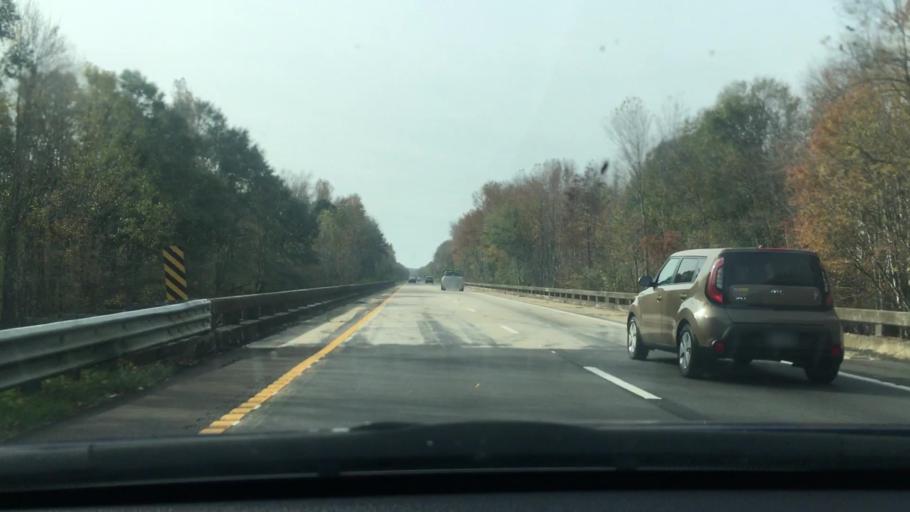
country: US
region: South Carolina
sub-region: Sumter County
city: Stateburg
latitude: 33.9512
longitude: -80.5926
